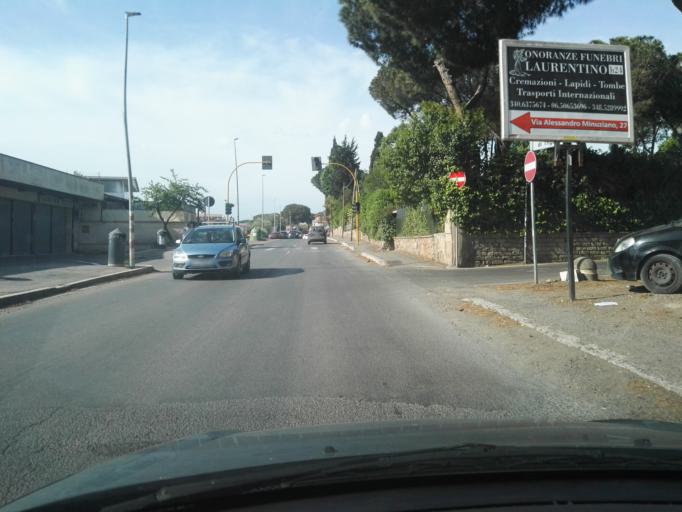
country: IT
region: Latium
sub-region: Citta metropolitana di Roma Capitale
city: Selcetta
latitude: 41.7687
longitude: 12.4785
